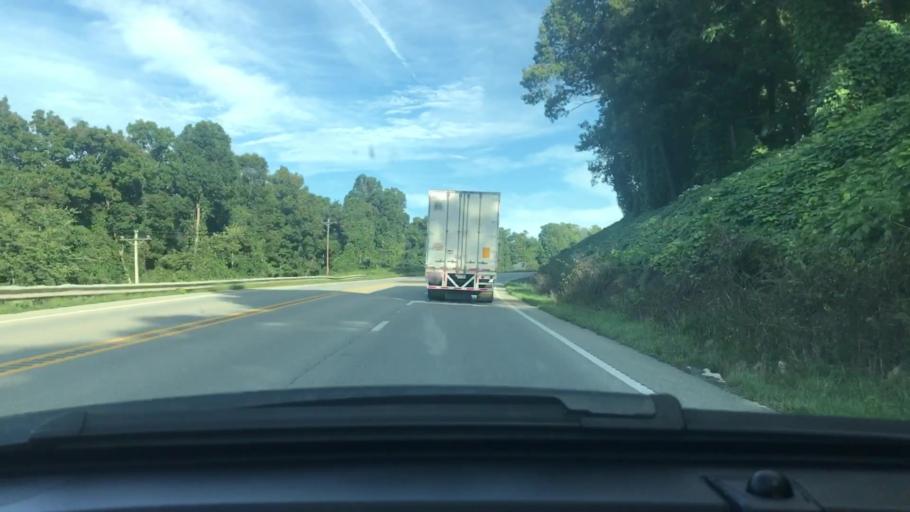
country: US
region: Arkansas
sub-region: Sharp County
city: Cherokee Village
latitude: 36.3004
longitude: -91.4082
